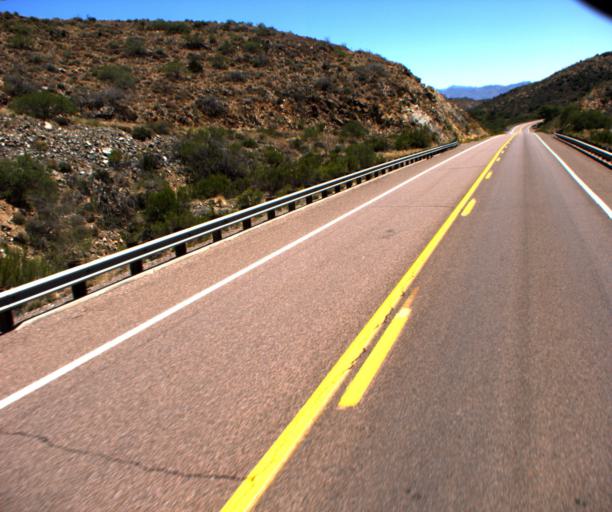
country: US
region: Arizona
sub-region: Yavapai County
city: Bagdad
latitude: 34.5626
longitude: -113.1673
